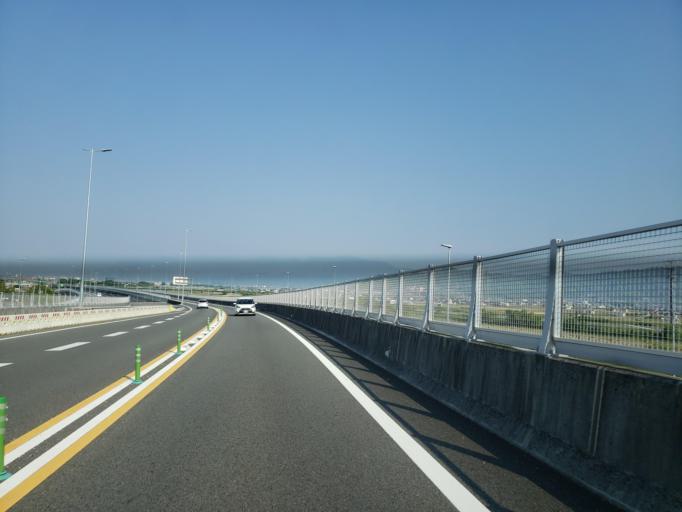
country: JP
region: Ehime
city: Masaki-cho
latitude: 33.8073
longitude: 132.7399
